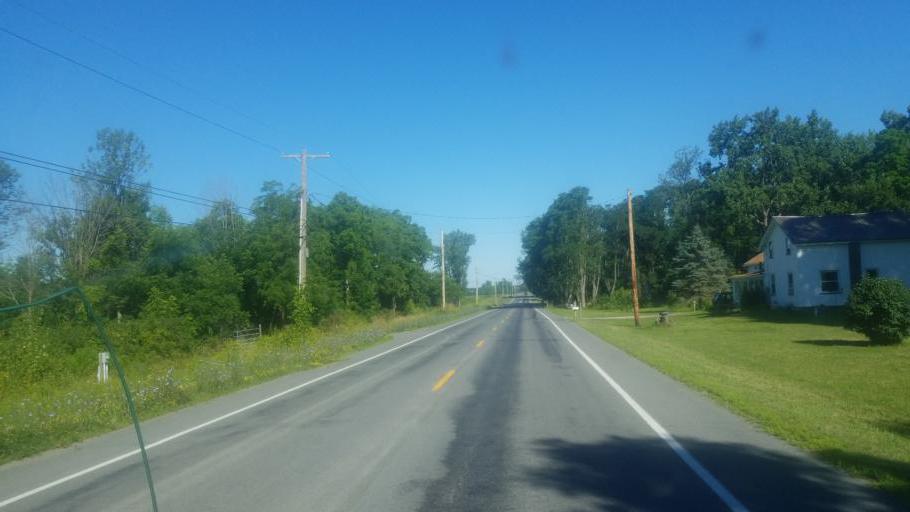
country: US
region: New York
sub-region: Ontario County
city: Canandaigua
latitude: 42.8379
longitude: -77.2176
